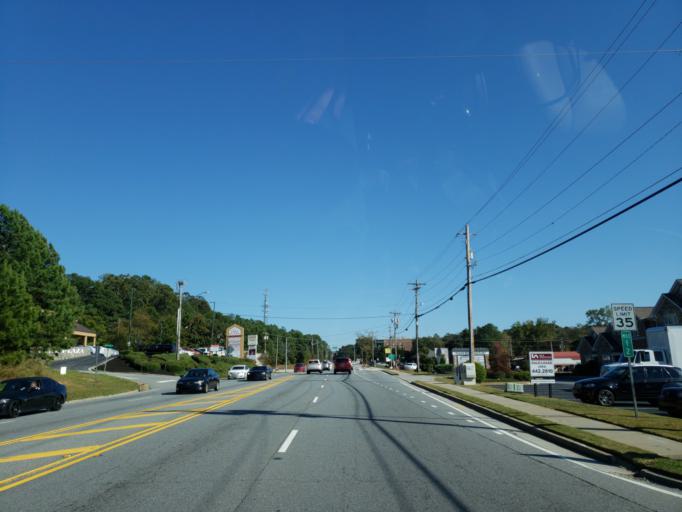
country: US
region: Georgia
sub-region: Gwinnett County
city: Lawrenceville
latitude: 33.9579
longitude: -83.9995
